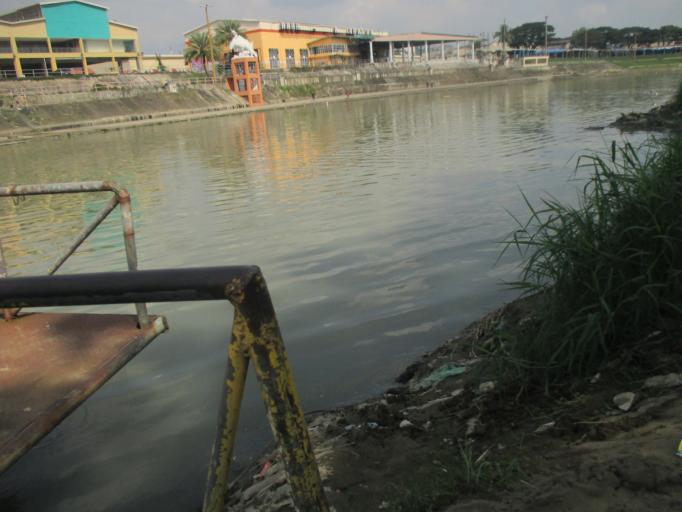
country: PH
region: Metro Manila
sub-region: Marikina
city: Calumpang
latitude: 14.6284
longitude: 121.0832
